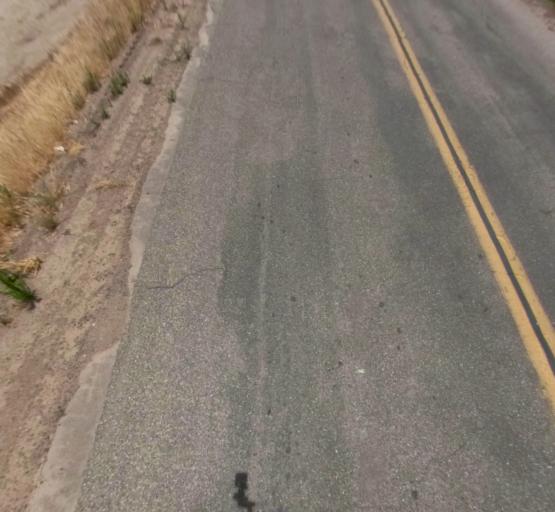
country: US
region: California
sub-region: Madera County
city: Parkwood
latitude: 36.8973
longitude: -120.0923
